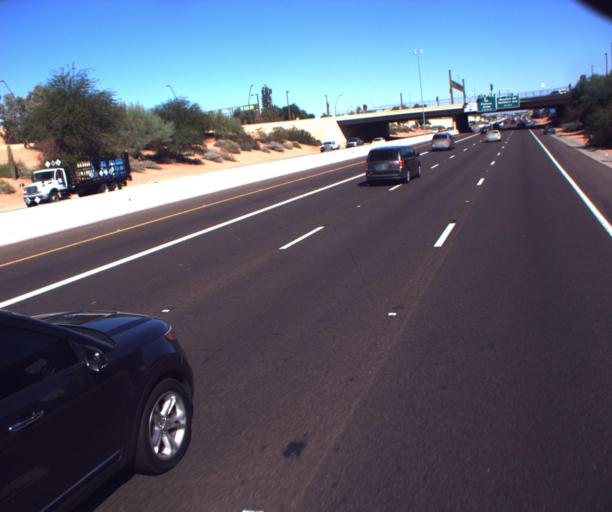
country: US
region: Arizona
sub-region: Maricopa County
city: San Carlos
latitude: 33.3623
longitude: -111.8938
